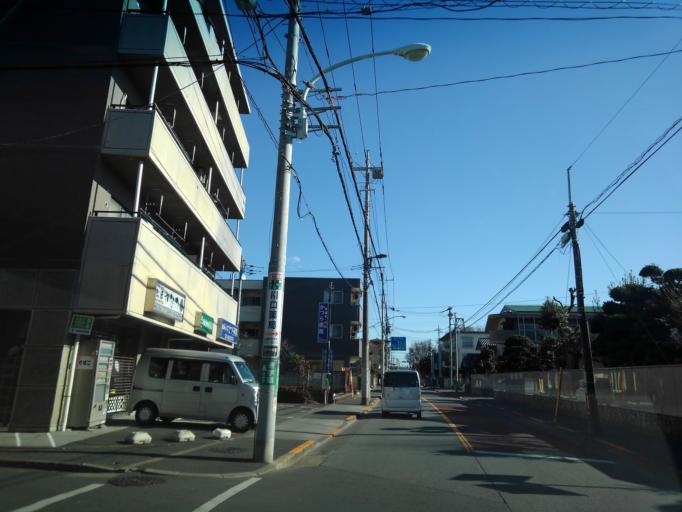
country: JP
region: Tokyo
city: Chofugaoka
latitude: 35.6665
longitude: 139.5137
